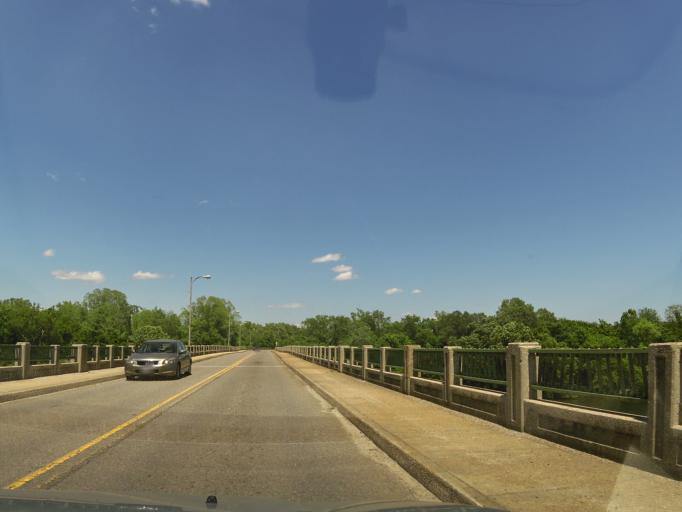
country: US
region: Georgia
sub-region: Richmond County
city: Augusta
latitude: 33.4763
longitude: -81.9572
